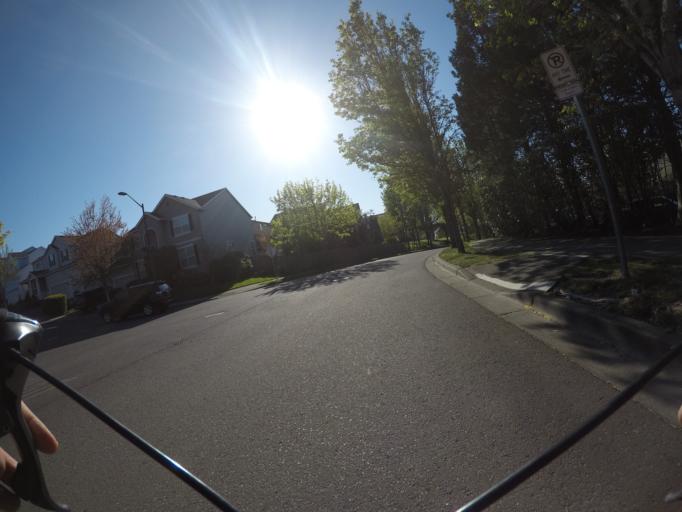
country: US
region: Oregon
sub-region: Washington County
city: King City
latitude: 45.4195
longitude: -122.8443
